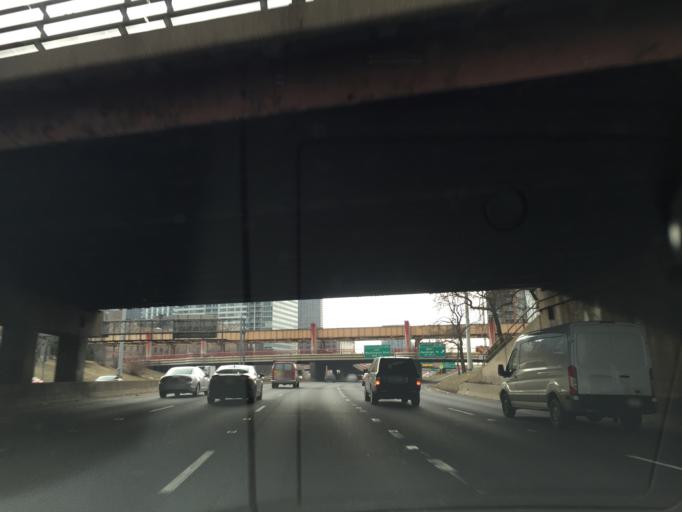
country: US
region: Illinois
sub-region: Cook County
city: Chicago
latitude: 41.8872
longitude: -87.6468
